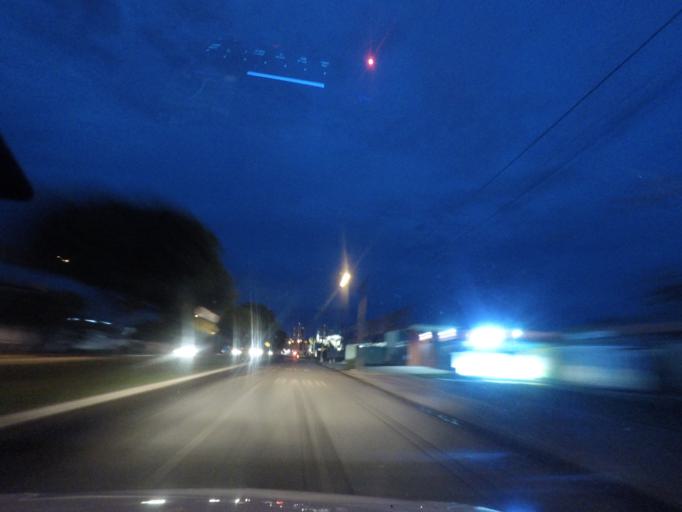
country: BR
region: Goias
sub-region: Goiania
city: Goiania
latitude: -16.7018
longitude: -49.3266
